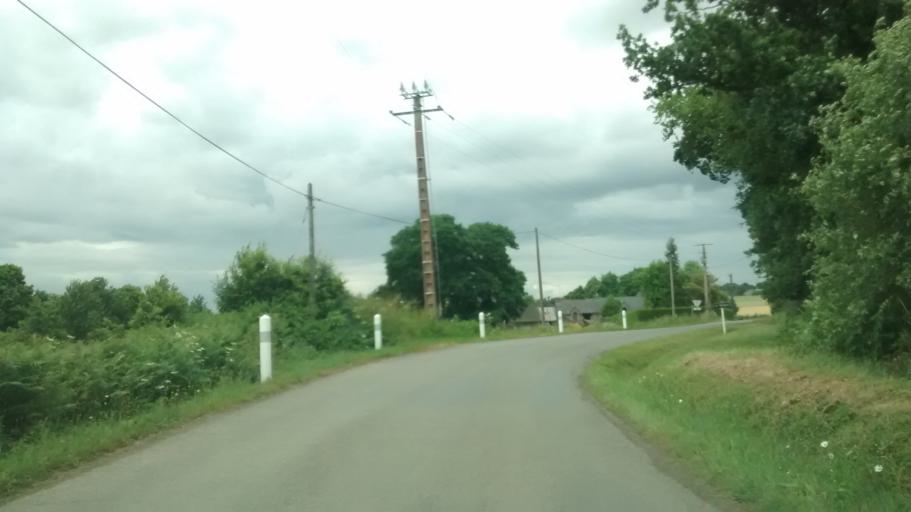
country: FR
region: Brittany
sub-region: Departement d'Ille-et-Vilaine
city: Sixt-sur-Aff
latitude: 47.7913
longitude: -2.1059
